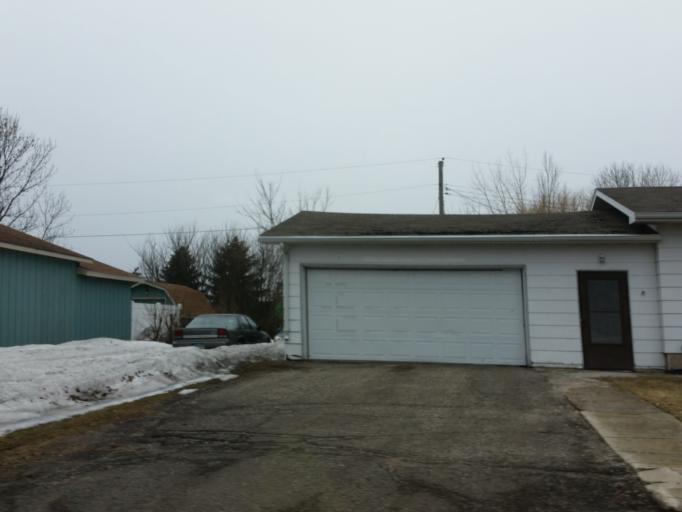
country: US
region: North Dakota
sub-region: Walsh County
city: Grafton
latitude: 48.5594
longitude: -97.1833
